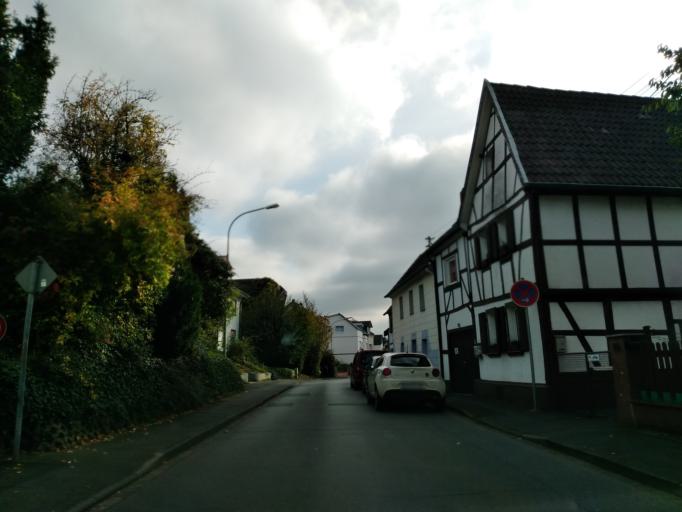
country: DE
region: North Rhine-Westphalia
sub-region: Regierungsbezirk Koln
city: Konigswinter
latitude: 50.6956
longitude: 7.1881
